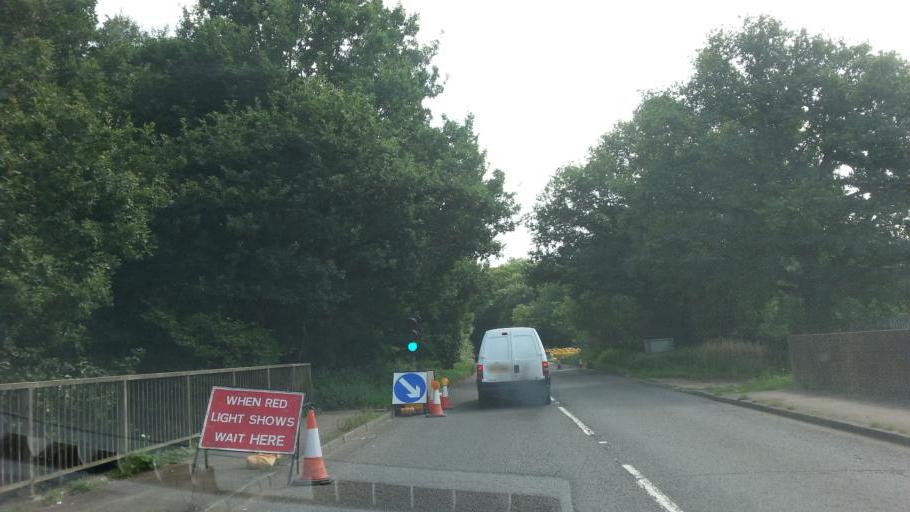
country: GB
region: England
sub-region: Surrey
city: Woking
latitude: 51.3360
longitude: -0.5781
